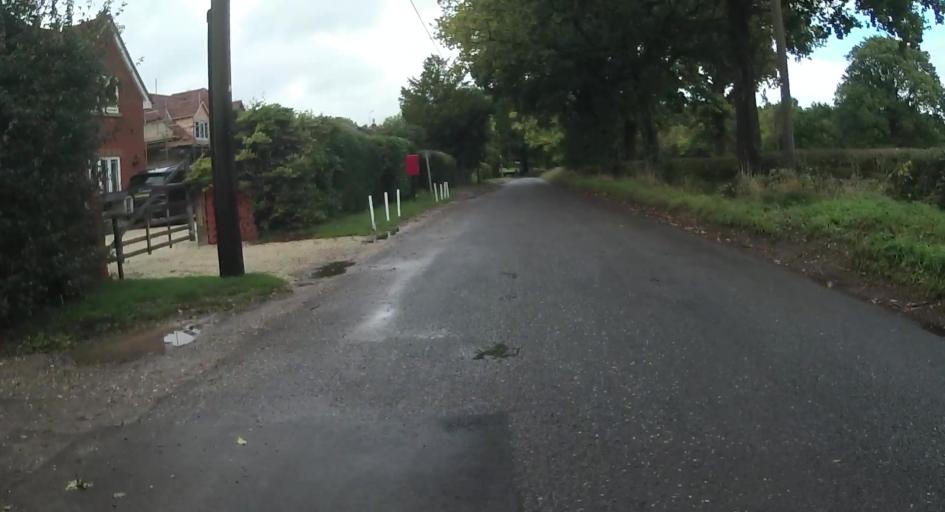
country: GB
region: England
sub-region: Hampshire
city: Tadley
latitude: 51.3212
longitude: -1.1564
